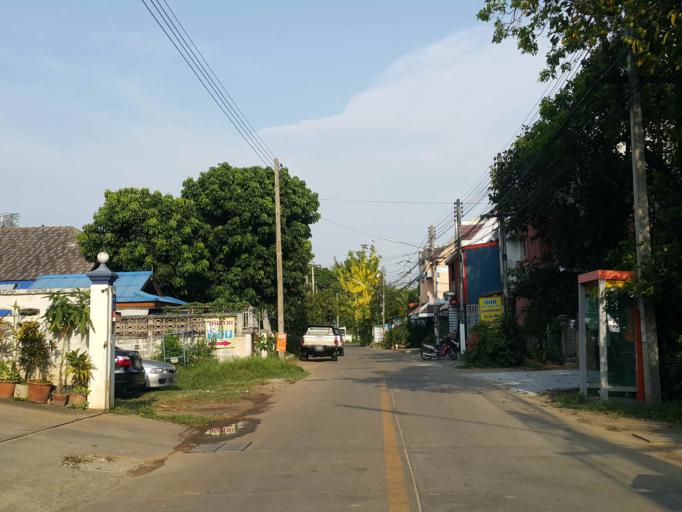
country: TH
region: Chiang Mai
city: Chiang Mai
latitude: 18.7653
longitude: 99.0269
